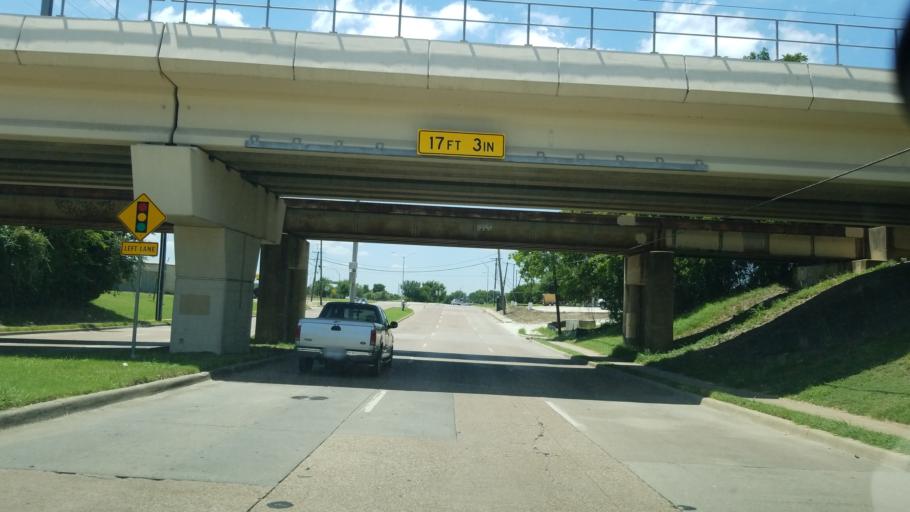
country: US
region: Texas
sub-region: Dallas County
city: Hutchins
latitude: 32.7344
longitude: -96.7100
